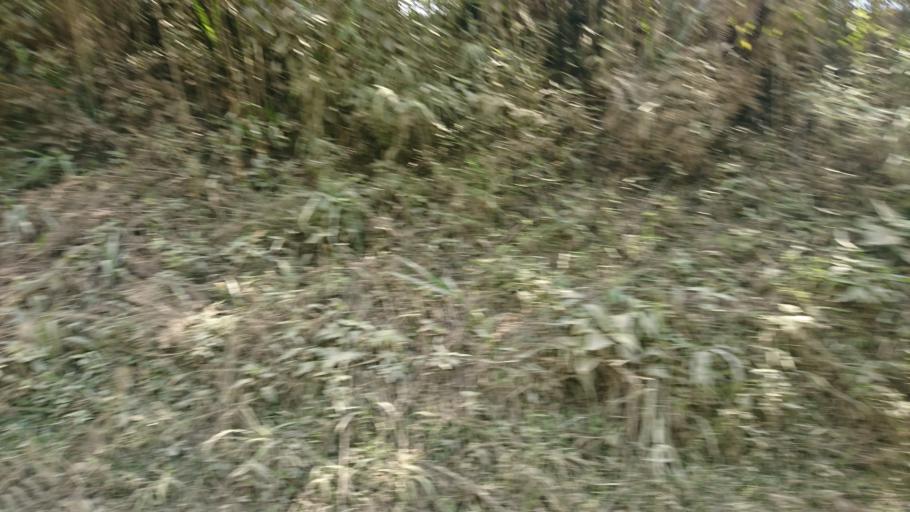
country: BO
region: La Paz
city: Coroico
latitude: -16.1288
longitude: -67.7577
